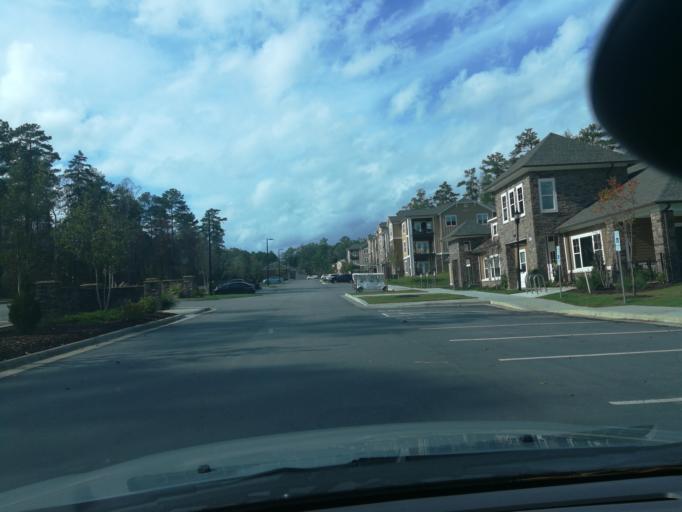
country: US
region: North Carolina
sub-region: Durham County
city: Durham
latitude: 36.0576
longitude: -78.9393
